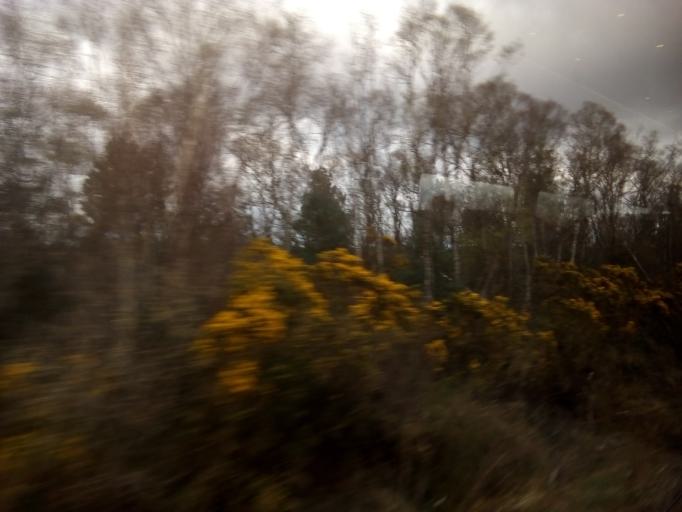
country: IE
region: Leinster
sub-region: An Longfort
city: Longford
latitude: 53.8066
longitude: -7.8614
